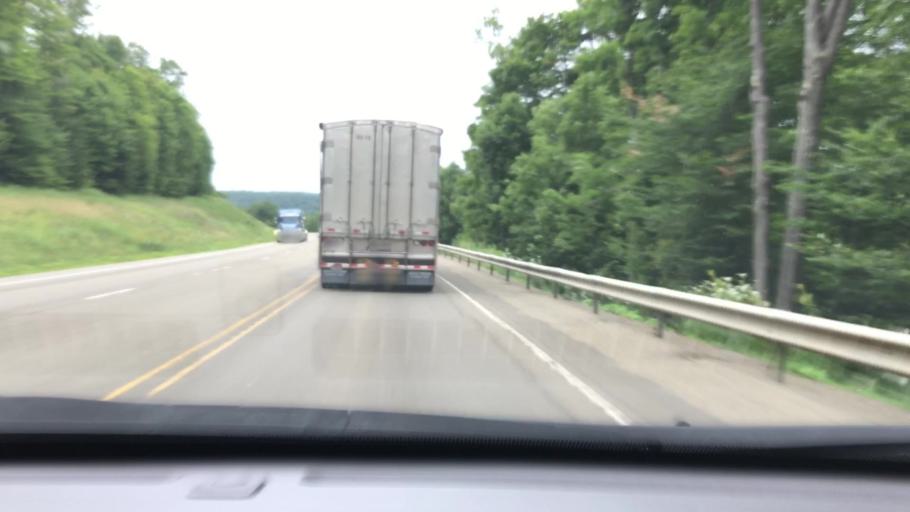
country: US
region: Pennsylvania
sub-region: McKean County
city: Kane
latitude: 41.7447
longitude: -78.6858
